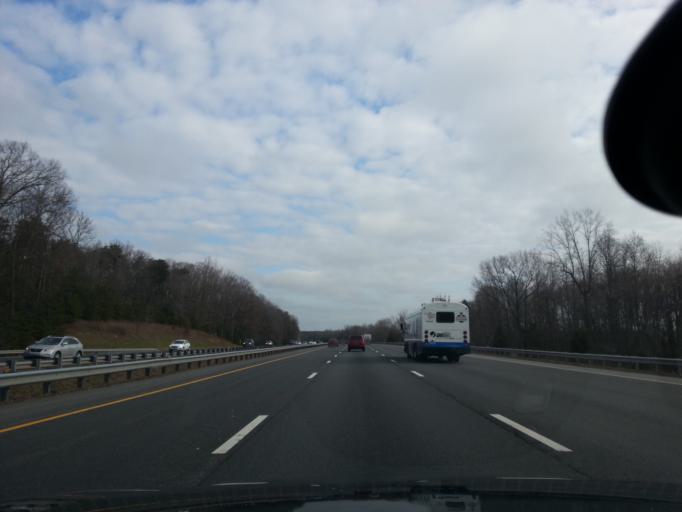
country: US
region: Virginia
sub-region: Spotsylvania County
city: Spotsylvania Courthouse
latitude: 38.1371
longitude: -77.5087
